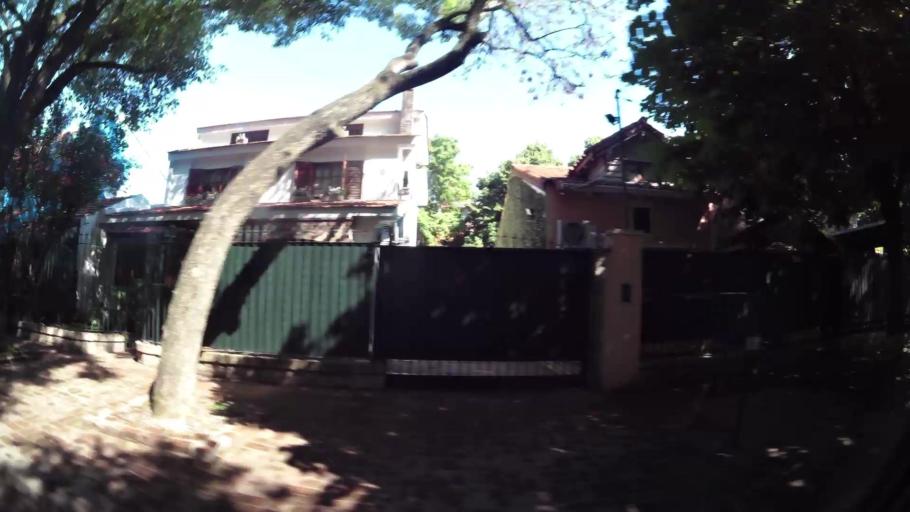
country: AR
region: Buenos Aires
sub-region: Partido de Tigre
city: Tigre
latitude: -34.4827
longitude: -58.5741
